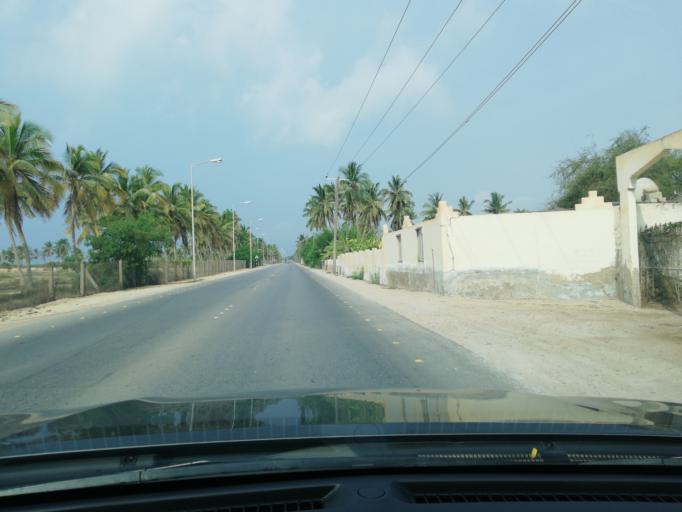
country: OM
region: Zufar
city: Salalah
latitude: 17.0120
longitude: 54.1427
